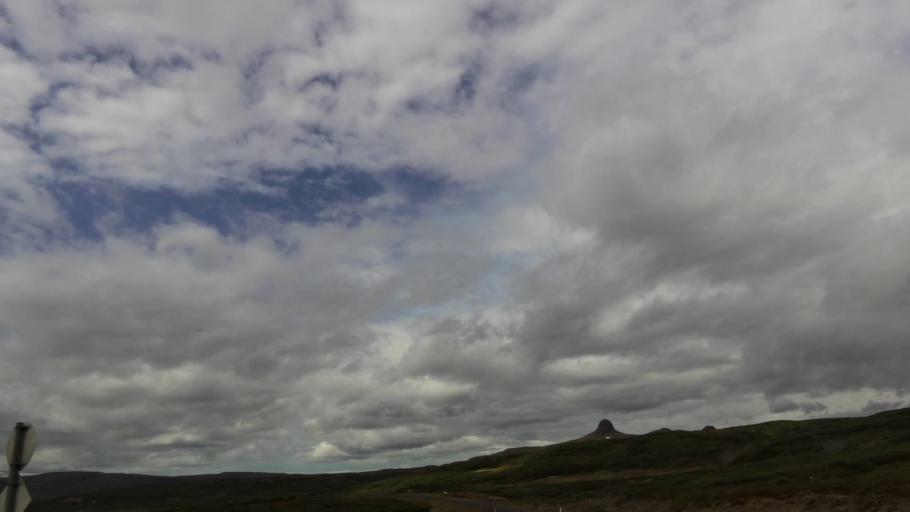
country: IS
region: West
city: Stykkisholmur
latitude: 65.5431
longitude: -22.0958
